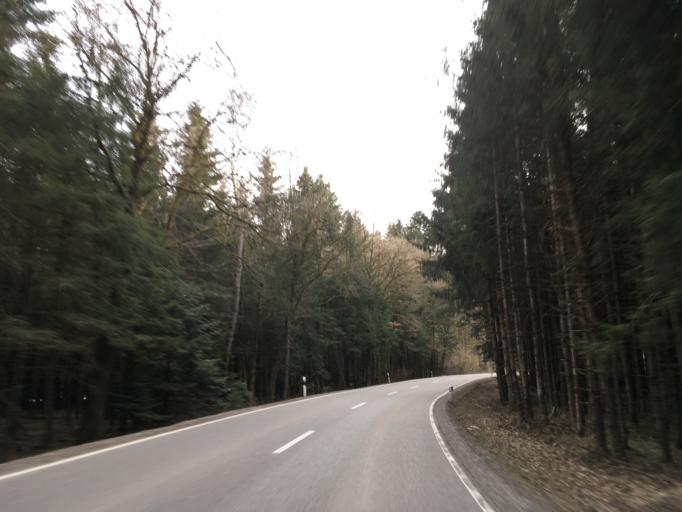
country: DE
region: Bavaria
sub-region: Upper Bavaria
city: Prutting
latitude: 47.9036
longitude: 12.2102
